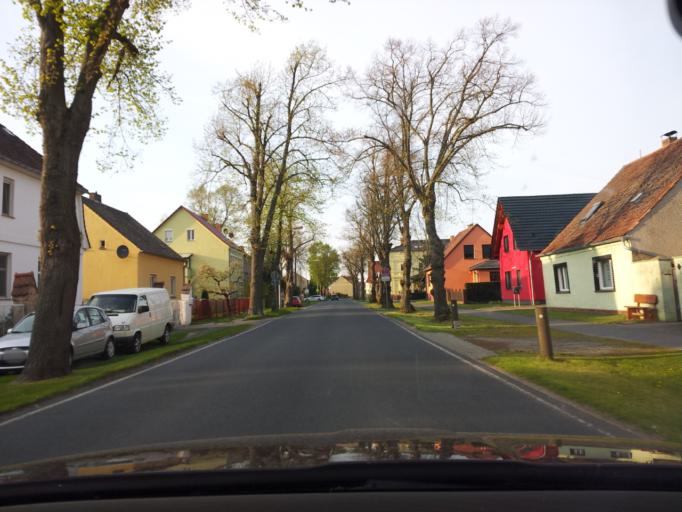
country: DE
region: Brandenburg
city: Dahme
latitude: 51.8643
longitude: 13.4185
